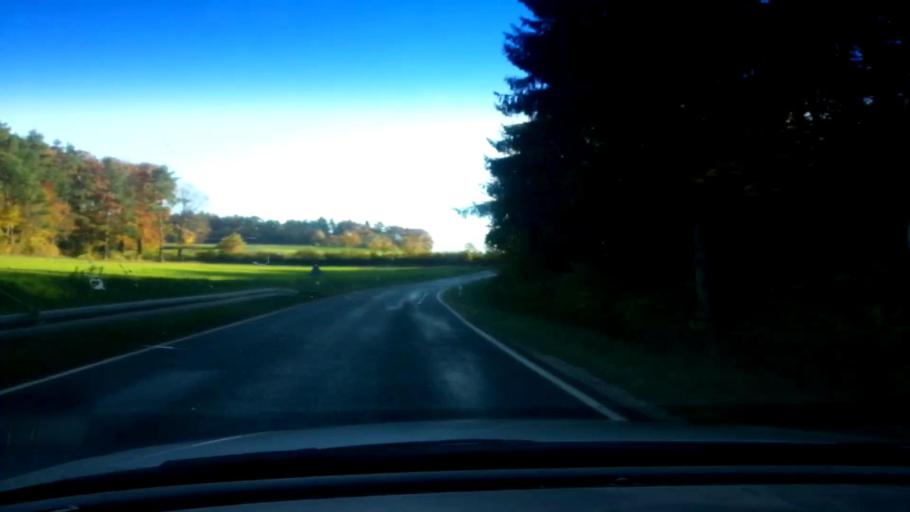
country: DE
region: Bavaria
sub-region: Upper Franconia
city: Poxdorf
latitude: 49.9186
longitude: 11.0897
